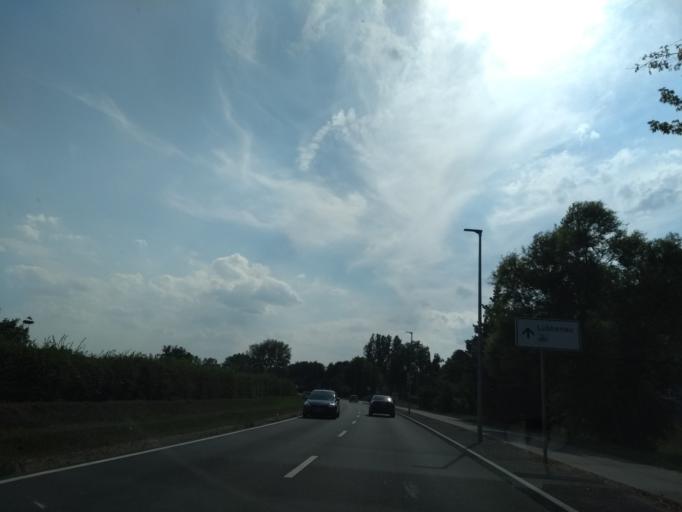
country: DE
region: Brandenburg
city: Lubbenau
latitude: 51.8576
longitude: 13.9641
